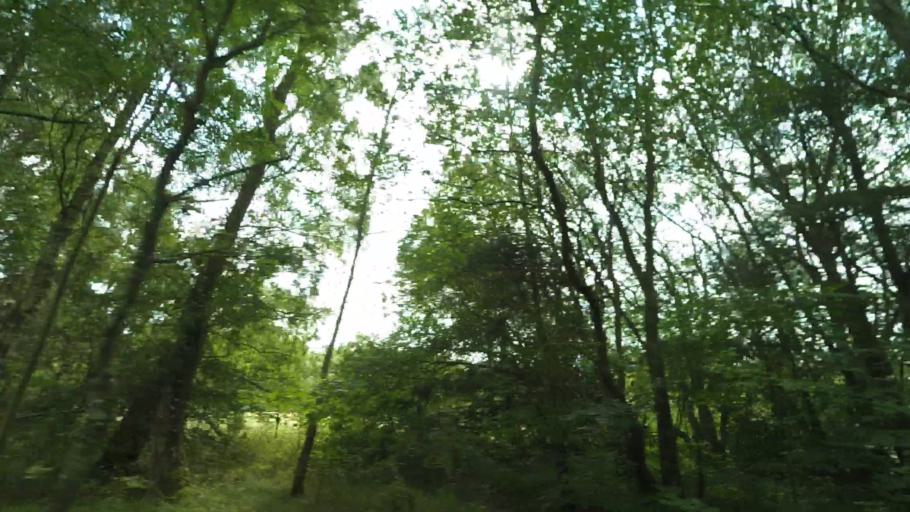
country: DK
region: Central Jutland
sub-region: Norddjurs Kommune
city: Allingabro
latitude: 56.5478
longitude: 10.3686
